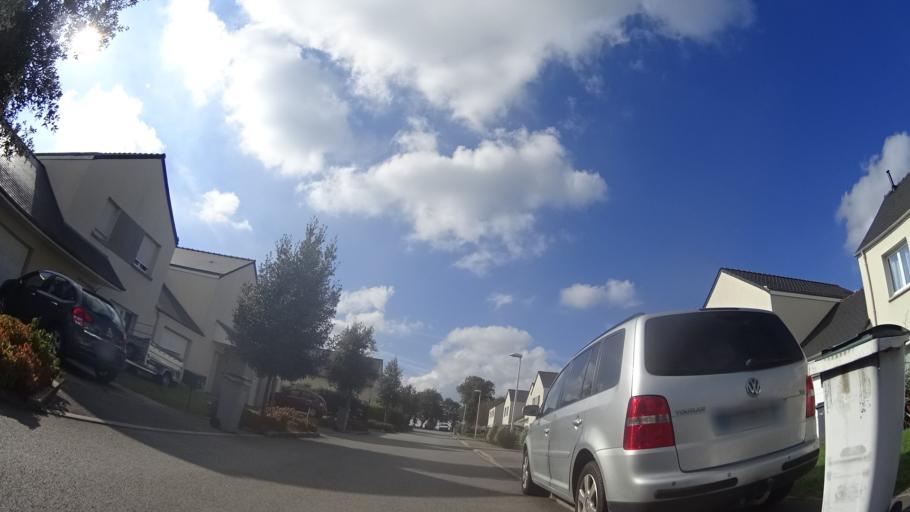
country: FR
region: Brittany
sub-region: Departement d'Ille-et-Vilaine
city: Geveze
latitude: 48.2238
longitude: -1.8029
